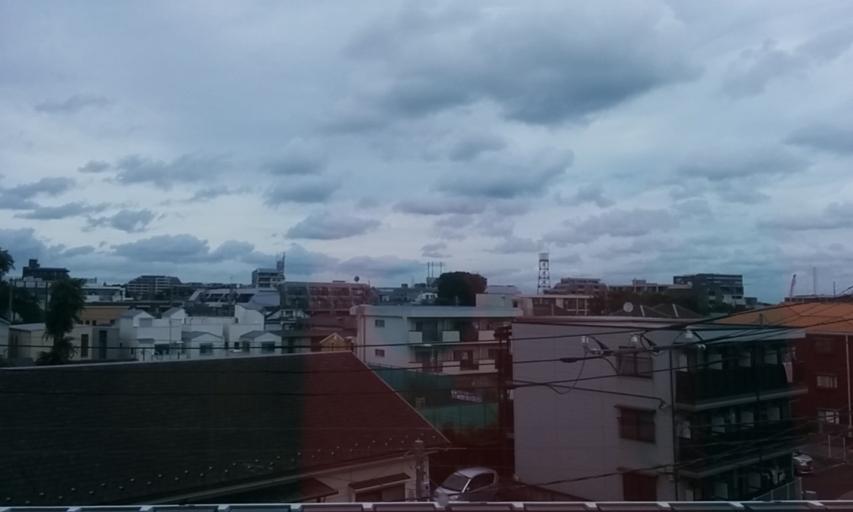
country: JP
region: Tokyo
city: Musashino
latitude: 35.7473
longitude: 139.5920
